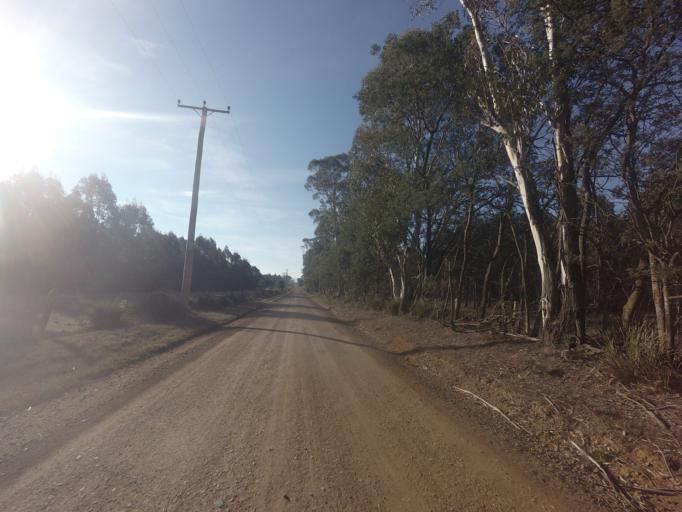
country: AU
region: Tasmania
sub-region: Brighton
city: Bridgewater
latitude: -42.4448
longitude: 147.3857
